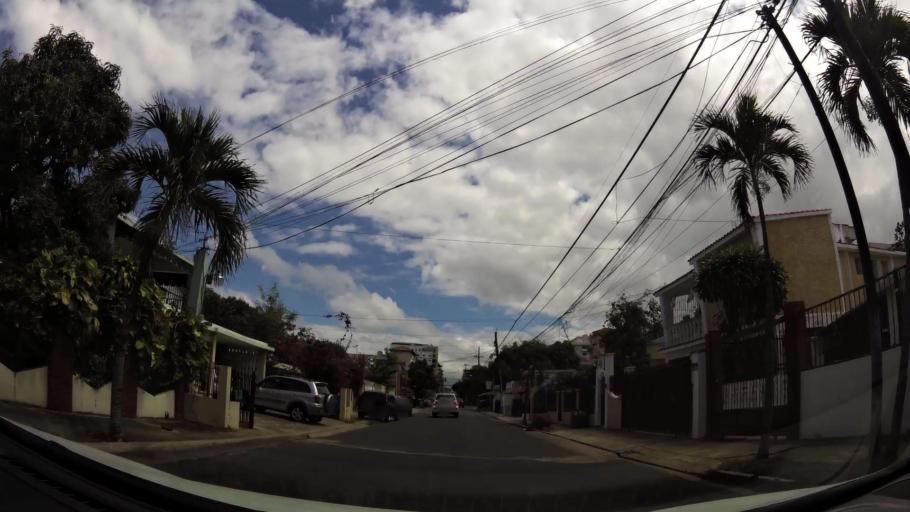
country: DO
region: Nacional
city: Bella Vista
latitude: 18.4594
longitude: -69.9493
